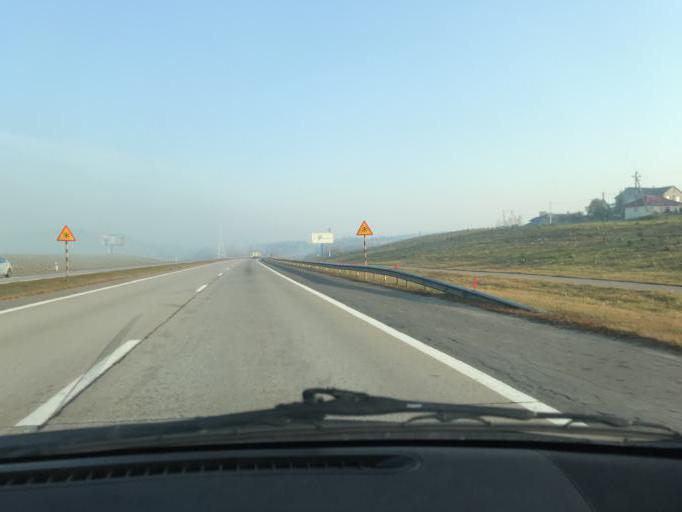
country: BY
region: Minsk
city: Borovlyany
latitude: 54.0110
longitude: 27.6588
